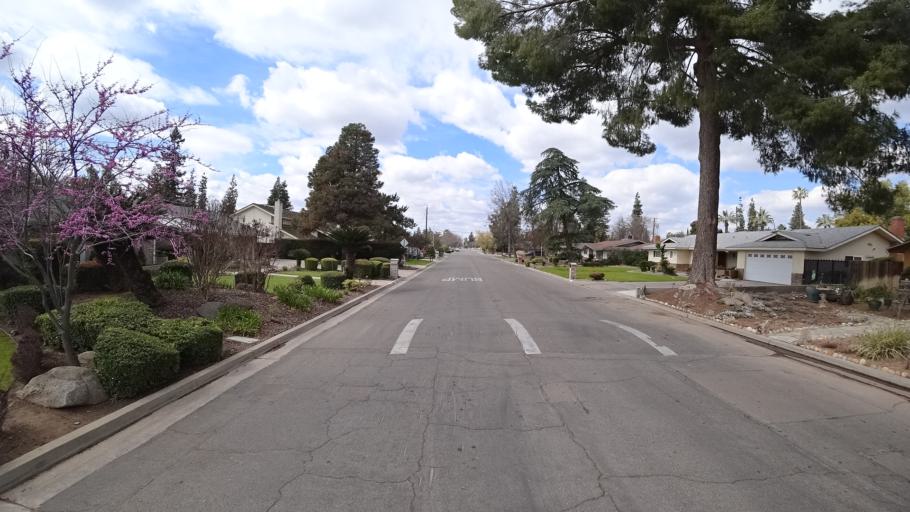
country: US
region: California
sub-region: Fresno County
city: Fresno
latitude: 36.8191
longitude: -119.8431
